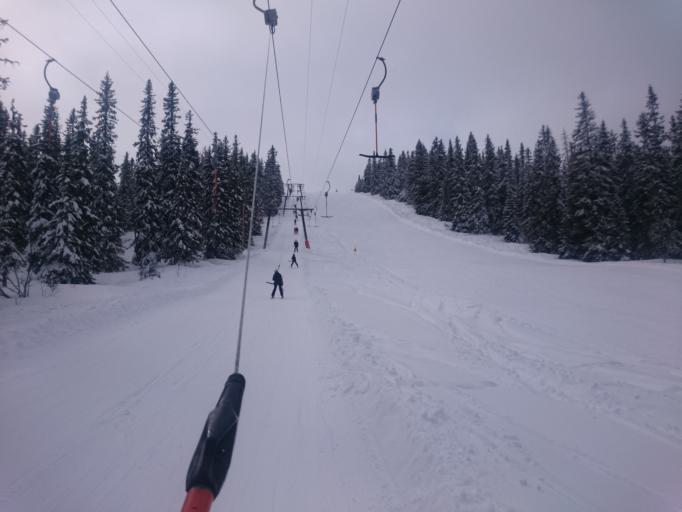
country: SE
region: Dalarna
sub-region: Malung-Saelens kommun
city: Malung
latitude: 61.1638
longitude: 13.1702
